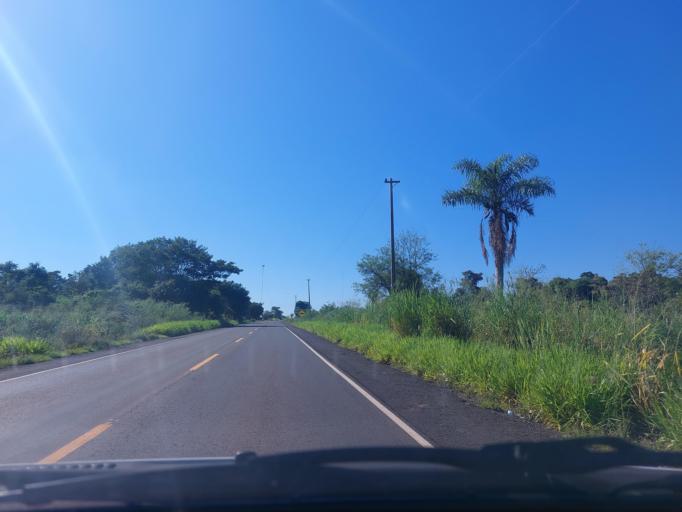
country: PY
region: San Pedro
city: Guayaybi
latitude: -24.3175
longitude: -56.1763
